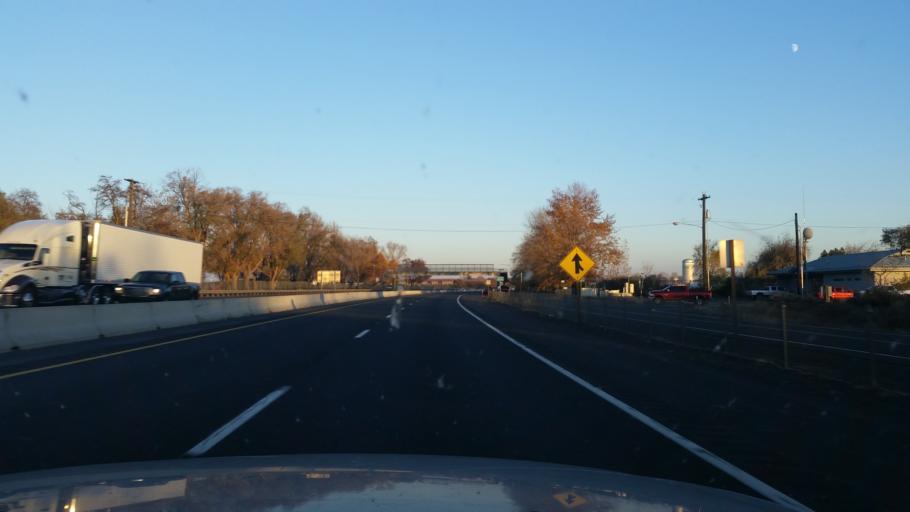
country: US
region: Washington
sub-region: Grant County
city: Cascade Valley
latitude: 47.1039
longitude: -119.3312
